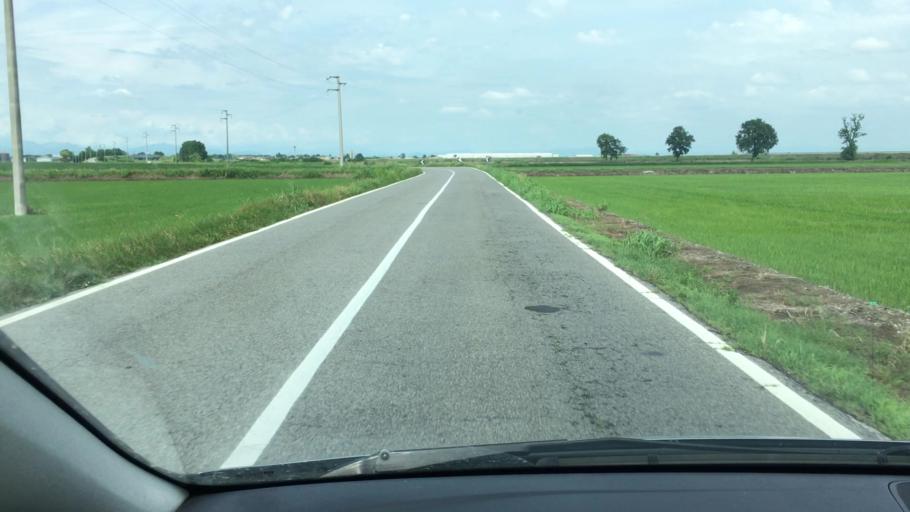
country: IT
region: Piedmont
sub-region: Provincia di Novara
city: Casalvolone
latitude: 45.4166
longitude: 8.4640
